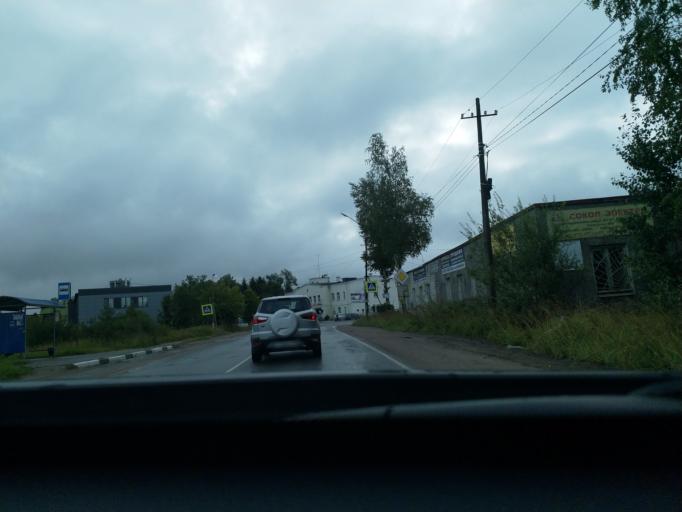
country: RU
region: Leningrad
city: Nikol'skoye
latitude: 59.6913
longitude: 30.8075
